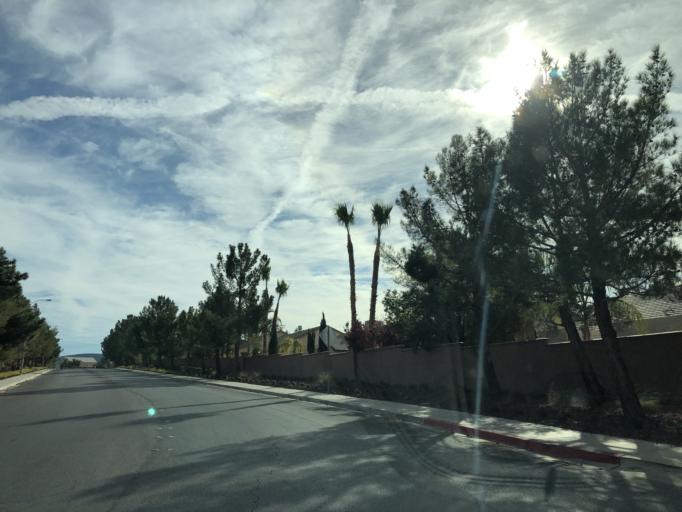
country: US
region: Nevada
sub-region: Clark County
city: Whitney
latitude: 36.0135
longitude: -115.0973
